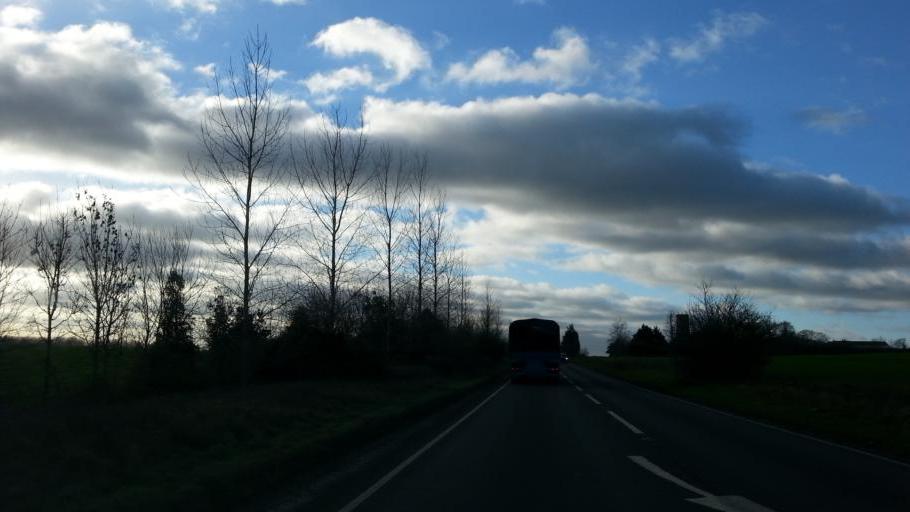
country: GB
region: England
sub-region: Norfolk
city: Harleston
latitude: 52.3648
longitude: 1.2162
